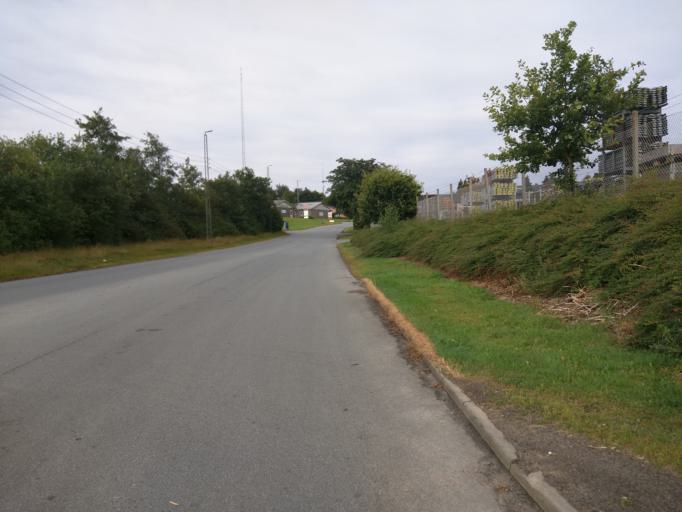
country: DK
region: Central Jutland
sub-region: Viborg Kommune
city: Viborg
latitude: 56.4508
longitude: 9.3802
